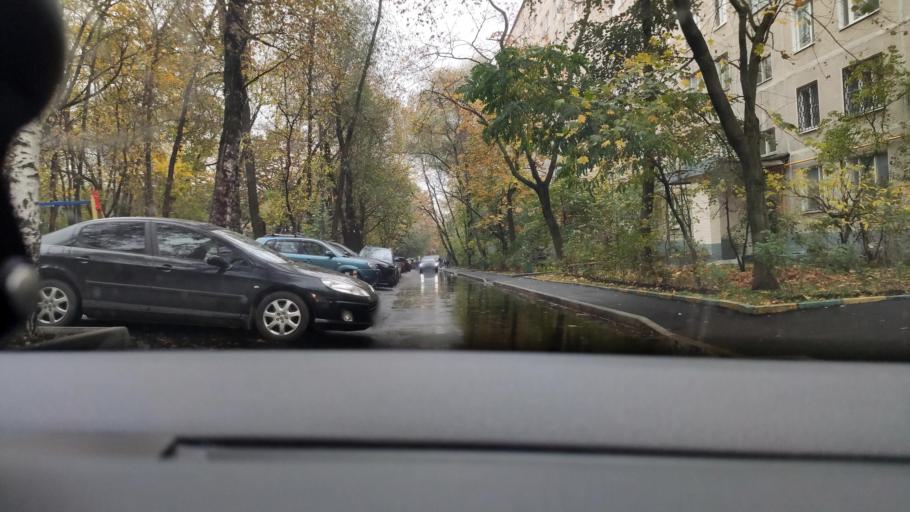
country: RU
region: Moskovskaya
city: Bol'shaya Setun'
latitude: 55.7323
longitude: 37.4421
